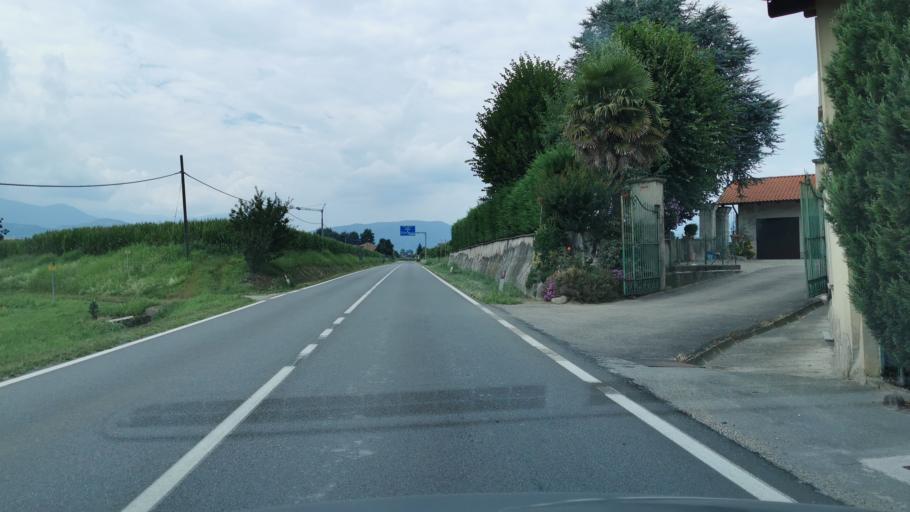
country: IT
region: Piedmont
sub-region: Provincia di Torino
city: Garzigliana
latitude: 44.8380
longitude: 7.3575
